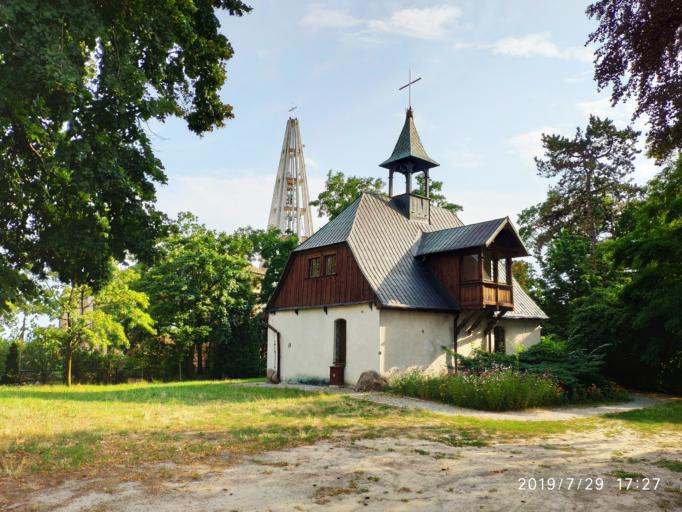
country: PL
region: Lubusz
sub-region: Zielona Gora
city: Zielona Gora
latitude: 51.9290
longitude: 15.5166
